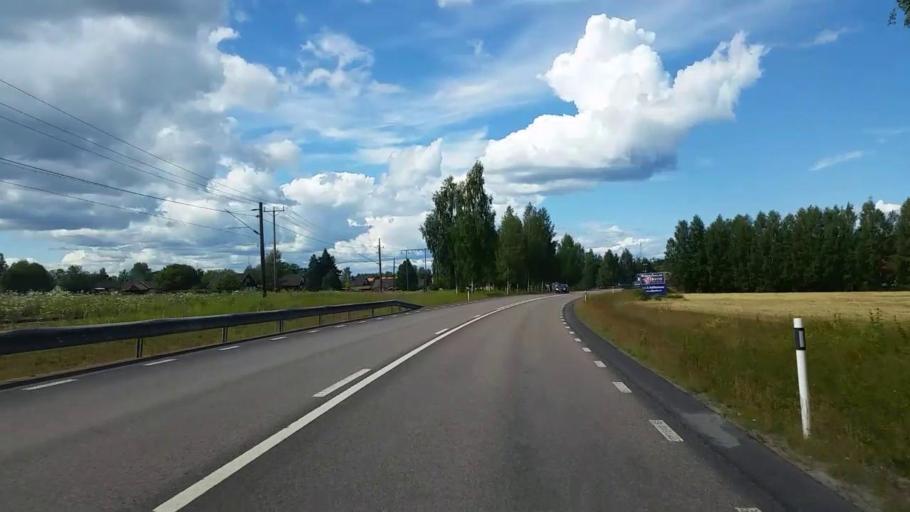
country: SE
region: Dalarna
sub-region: Leksand Municipality
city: Leksand
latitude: 60.7242
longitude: 15.0131
